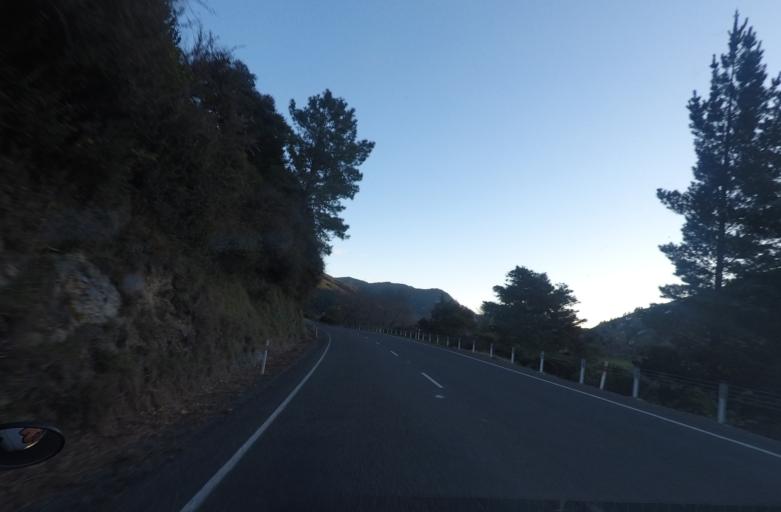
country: NZ
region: Marlborough
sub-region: Marlborough District
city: Picton
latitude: -41.2754
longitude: 173.7319
